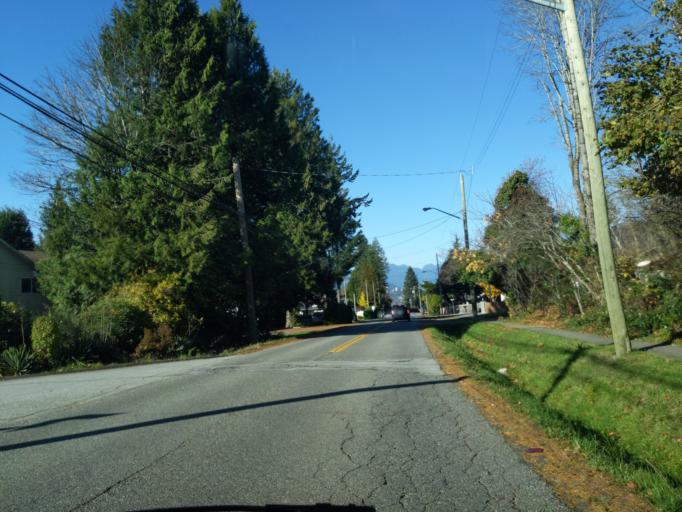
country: CA
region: British Columbia
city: New Westminster
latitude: 49.1944
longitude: -122.8661
